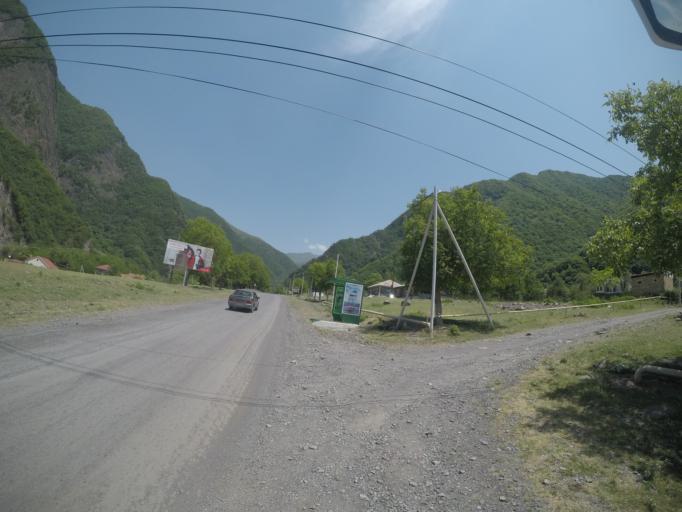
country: AZ
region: Qakh Rayon
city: Qaxbas
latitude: 41.4579
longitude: 47.0249
